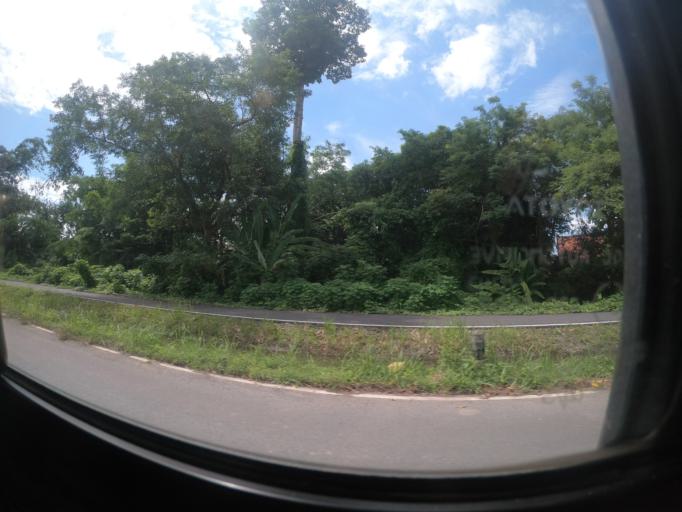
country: TH
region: Nakhon Nayok
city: Nakhon Nayok
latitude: 14.3061
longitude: 101.3121
